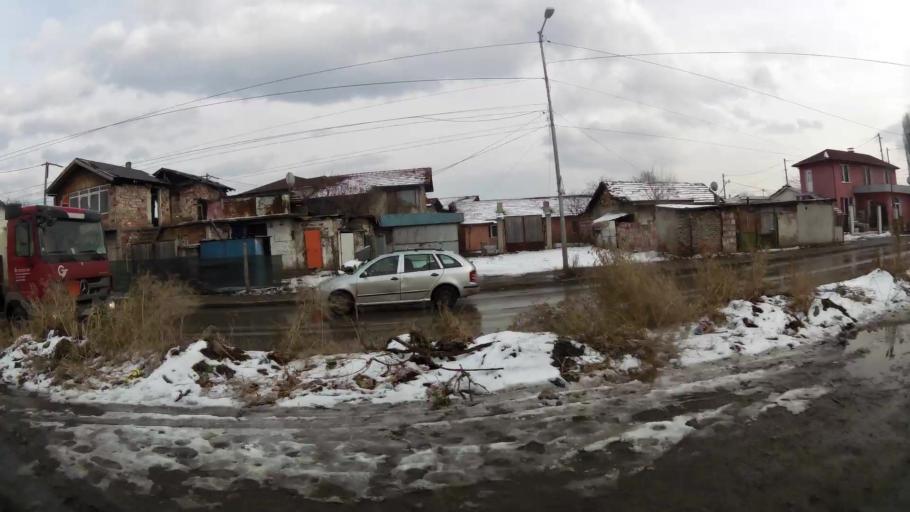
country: BG
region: Sofia-Capital
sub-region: Stolichna Obshtina
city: Sofia
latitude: 42.6940
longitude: 23.3827
